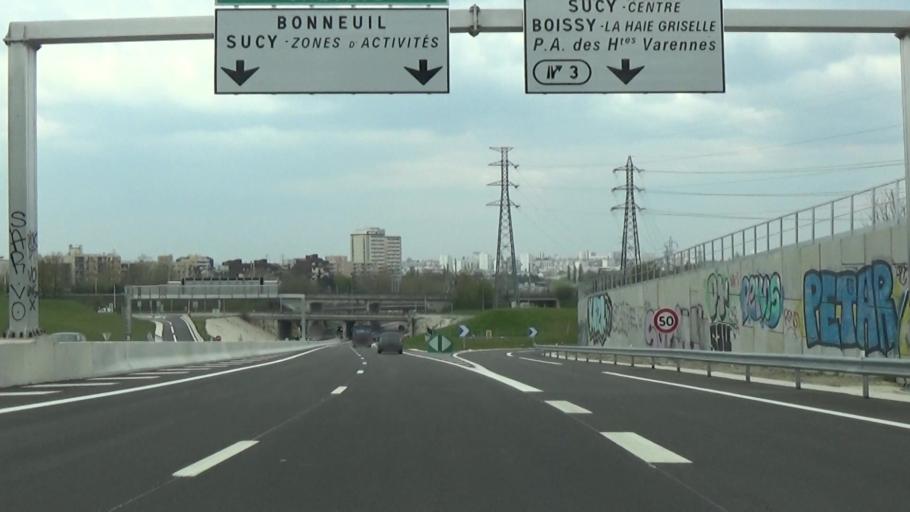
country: FR
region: Ile-de-France
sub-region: Departement du Val-de-Marne
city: Boissy-Saint-Leger
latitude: 48.7540
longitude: 2.5109
